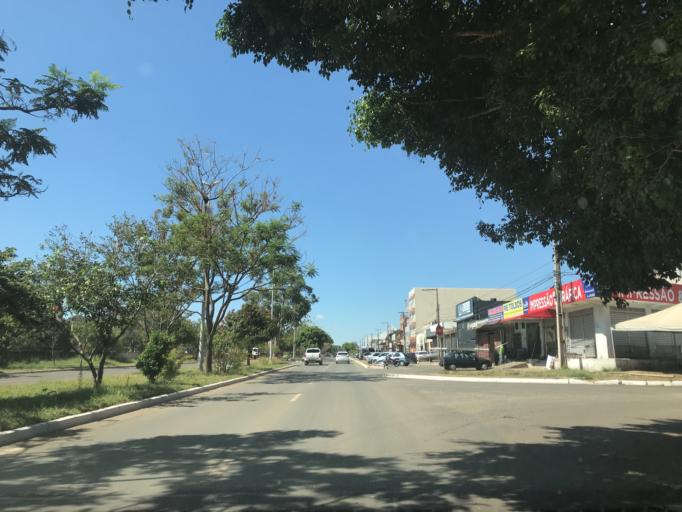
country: BR
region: Federal District
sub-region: Brasilia
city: Brasilia
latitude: -15.8028
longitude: -48.0921
